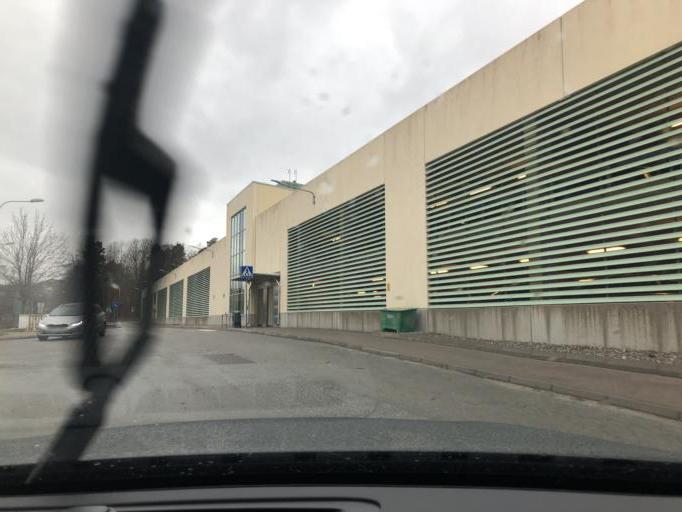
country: SE
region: Stockholm
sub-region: Sodertalje Kommun
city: Soedertaelje
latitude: 59.2055
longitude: 17.6104
